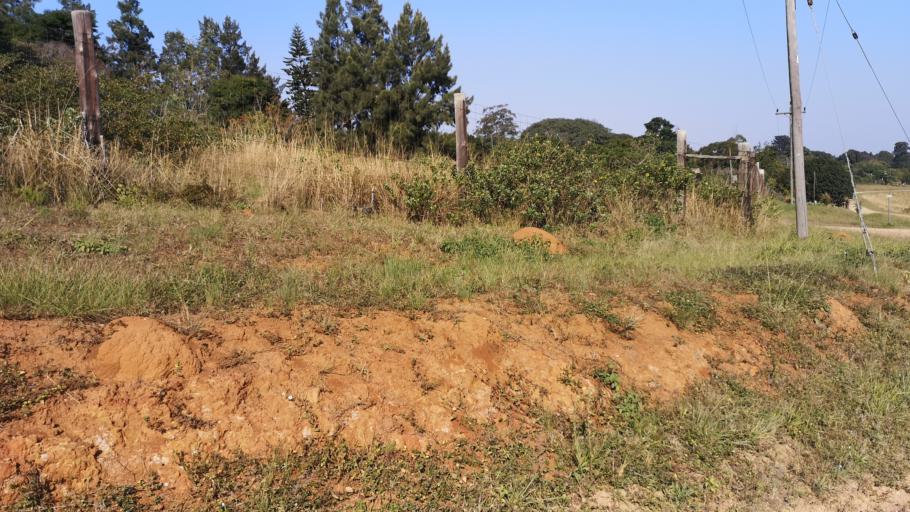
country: ZA
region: KwaZulu-Natal
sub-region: eThekwini Metropolitan Municipality
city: Mpumalanga
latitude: -29.7357
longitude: 30.6809
